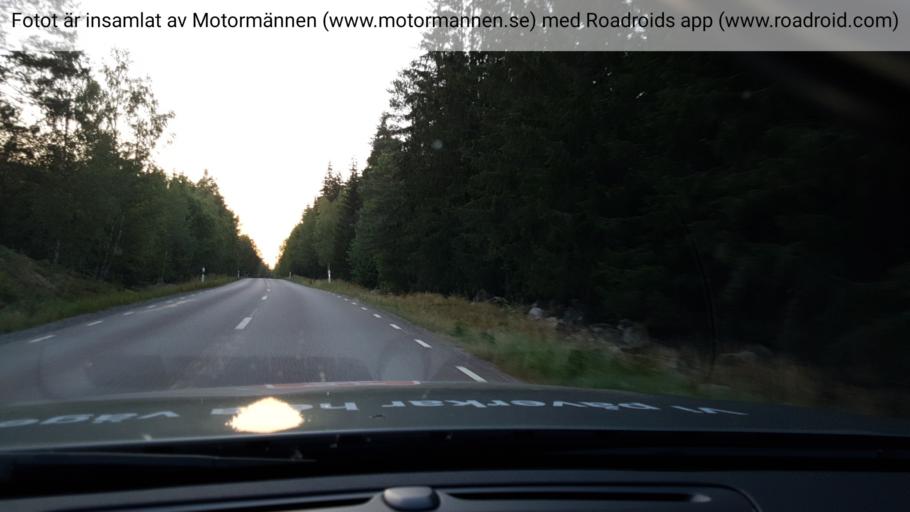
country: SE
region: Uppsala
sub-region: Heby Kommun
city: OEstervala
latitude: 60.0106
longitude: 17.2938
